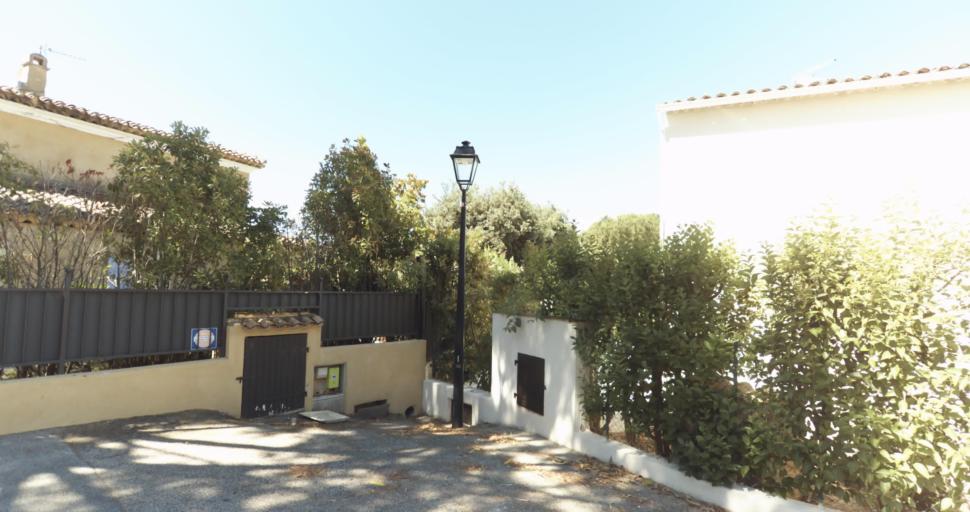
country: FR
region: Provence-Alpes-Cote d'Azur
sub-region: Departement du Var
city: Gassin
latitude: 43.2549
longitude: 6.5982
